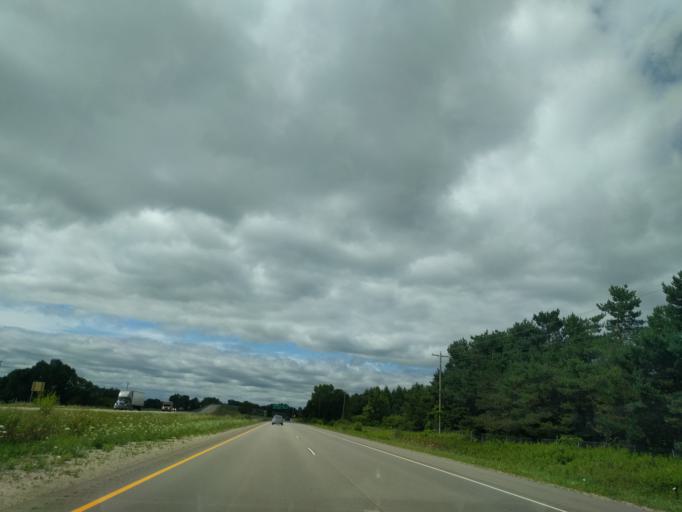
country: US
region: Wisconsin
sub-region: Oconto County
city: Oconto Falls
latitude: 44.7928
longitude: -88.0373
